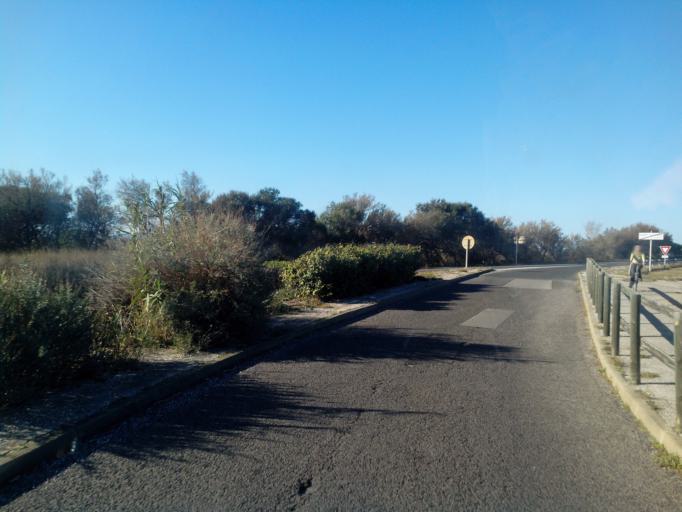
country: FR
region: Languedoc-Roussillon
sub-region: Departement de l'Aude
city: Leucate
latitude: 42.8516
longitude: 3.0360
